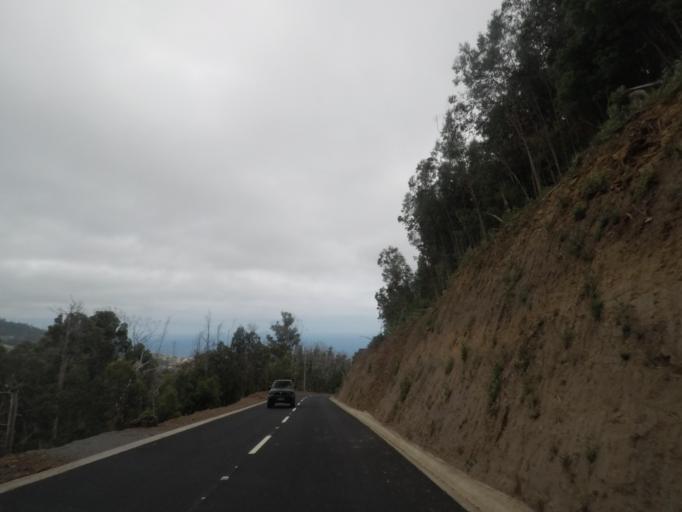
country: PT
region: Madeira
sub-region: Calheta
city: Estreito da Calheta
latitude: 32.7443
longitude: -17.1589
